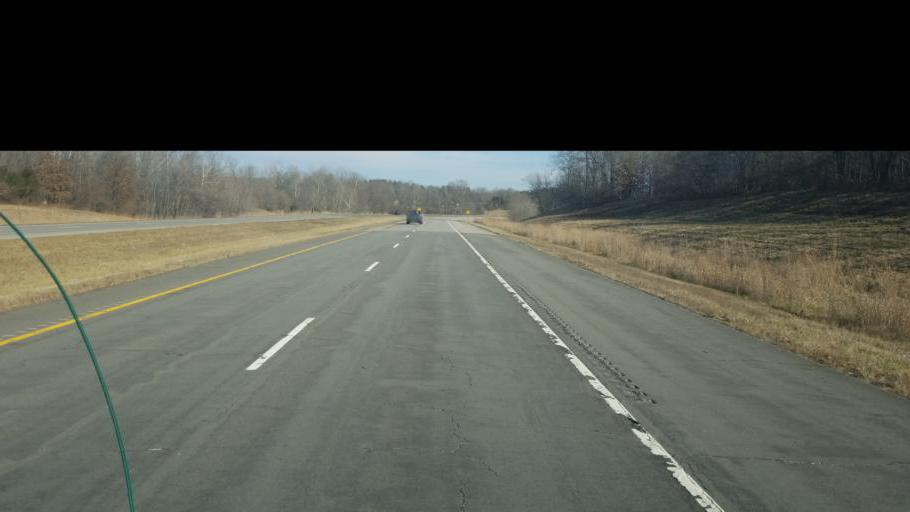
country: US
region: Illinois
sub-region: Saline County
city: Carrier Mills
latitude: 37.7369
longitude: -88.7172
